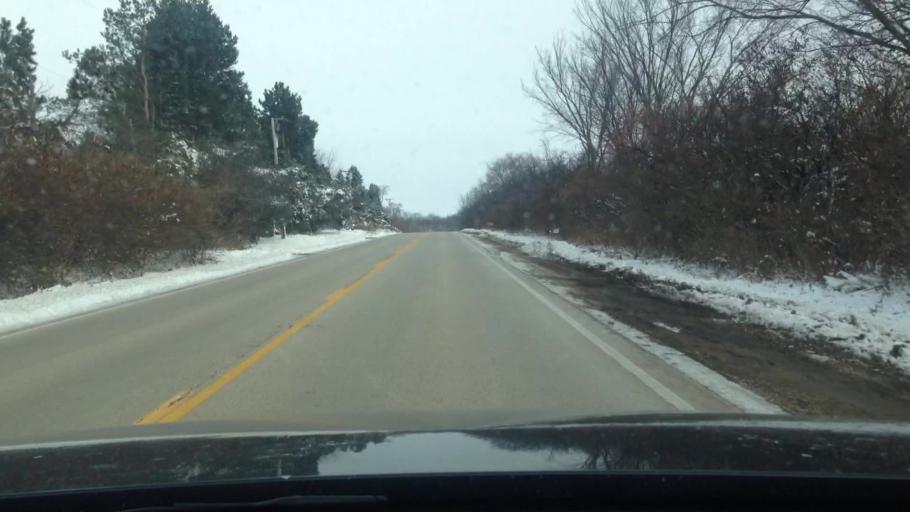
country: US
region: Illinois
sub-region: McHenry County
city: Woodstock
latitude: 42.3818
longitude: -88.4432
